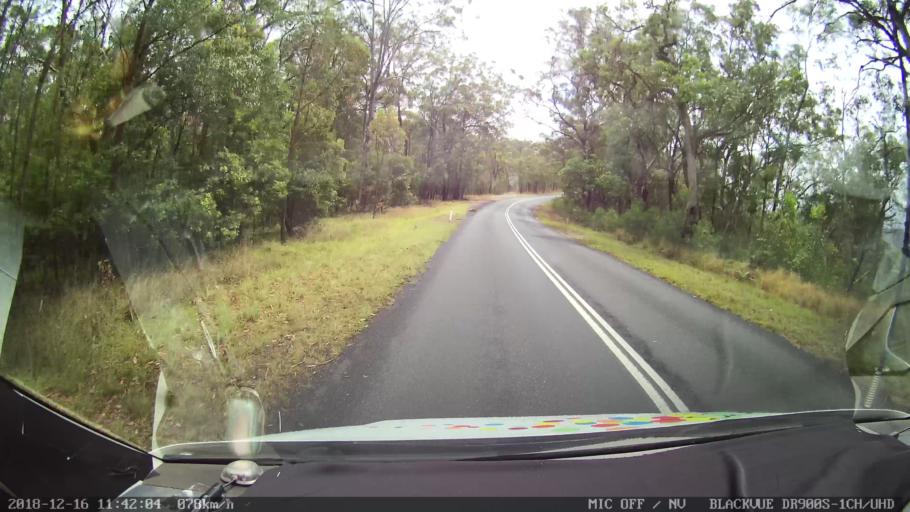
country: AU
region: New South Wales
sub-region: Tenterfield Municipality
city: Carrolls Creek
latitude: -28.9553
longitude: 152.2140
